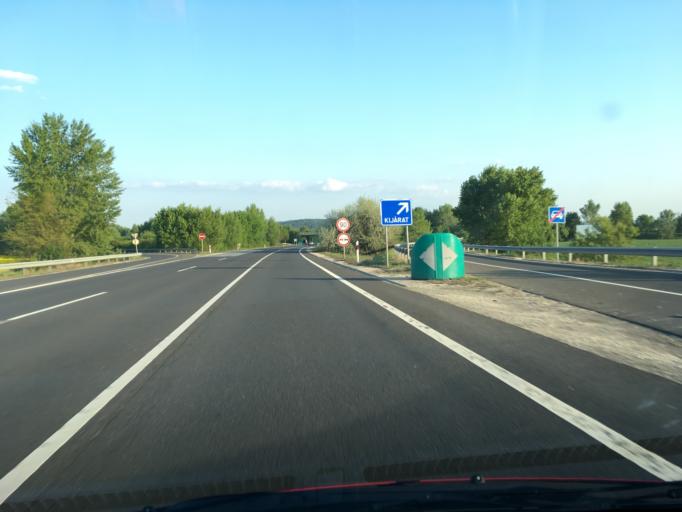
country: HU
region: Pest
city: Kosd
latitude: 47.7715
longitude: 19.1791
